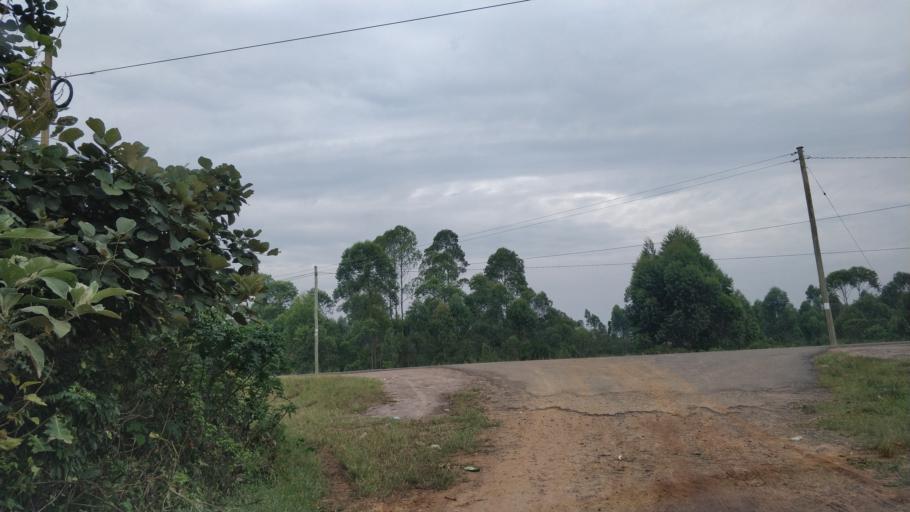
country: UG
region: Western Region
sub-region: Sheema District
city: Kibingo
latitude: -0.6939
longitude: 30.3896
